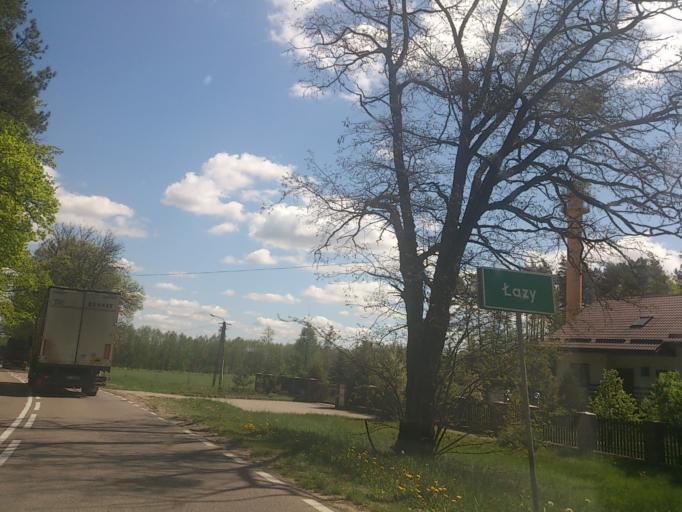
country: PL
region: Masovian Voivodeship
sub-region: Powiat makowski
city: Ploniawy-Bramura
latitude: 53.0175
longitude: 21.1063
